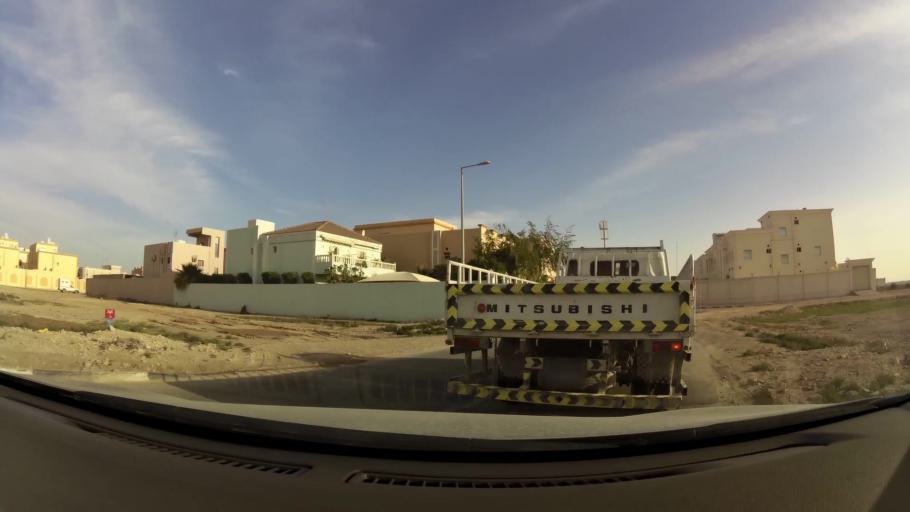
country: QA
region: Al Wakrah
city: Al Wakrah
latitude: 25.1434
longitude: 51.6138
